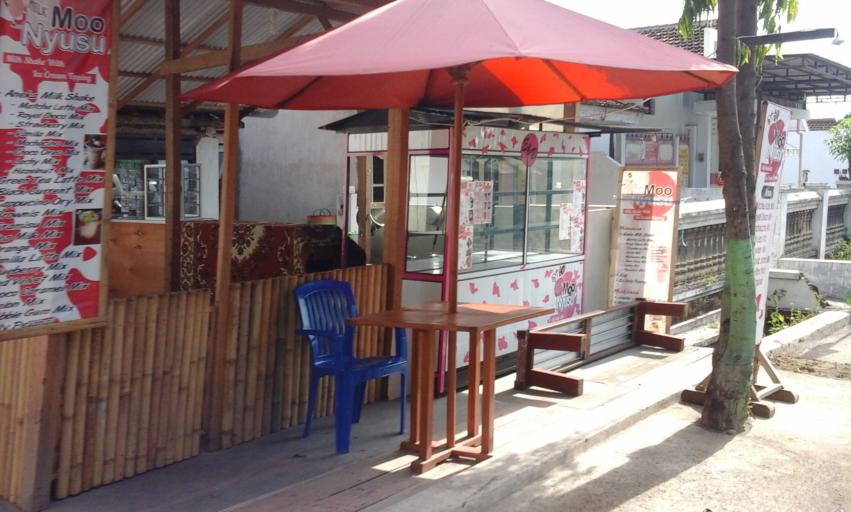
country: ID
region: East Java
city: Krajan
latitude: -8.2140
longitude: 114.3421
